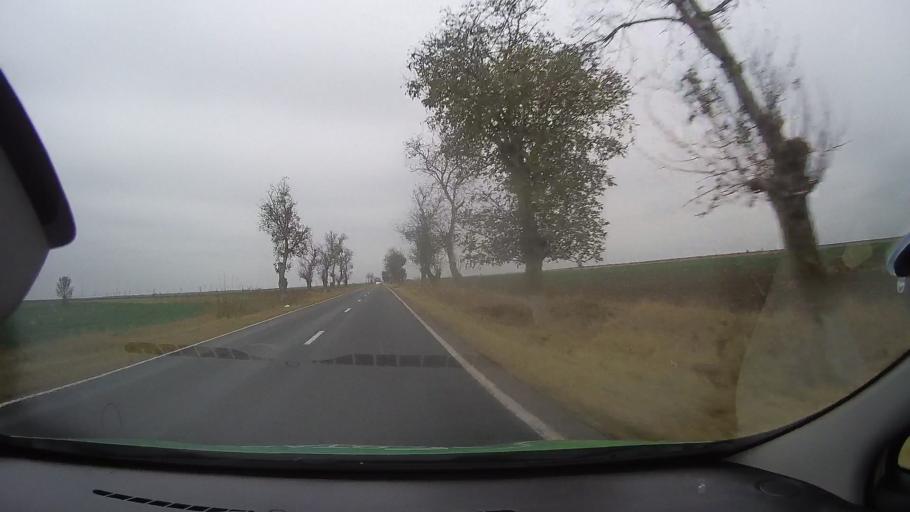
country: RO
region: Ialomita
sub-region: Comuna Scanteia
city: Scanteia
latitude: 44.7732
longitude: 27.4759
